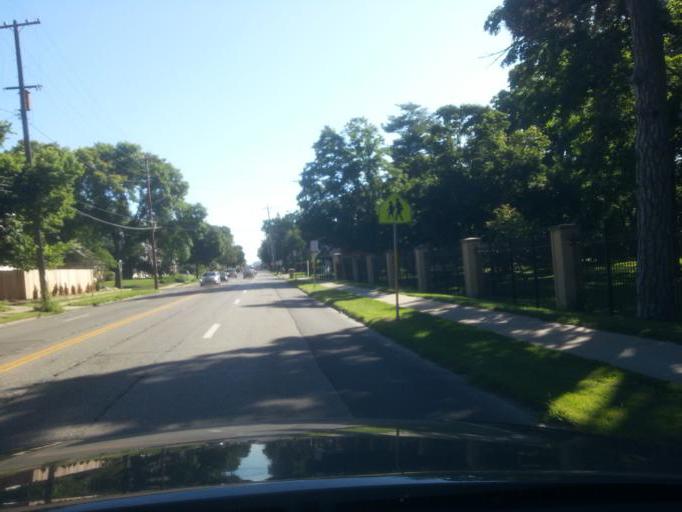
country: US
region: Wisconsin
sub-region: Dane County
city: Madison
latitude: 43.0618
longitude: -89.4218
